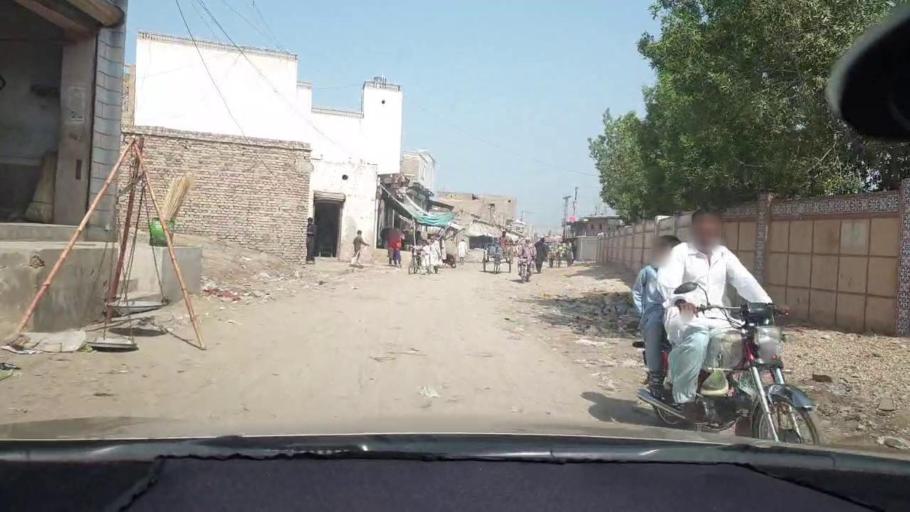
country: PK
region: Sindh
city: Kambar
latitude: 27.5822
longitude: 68.0044
